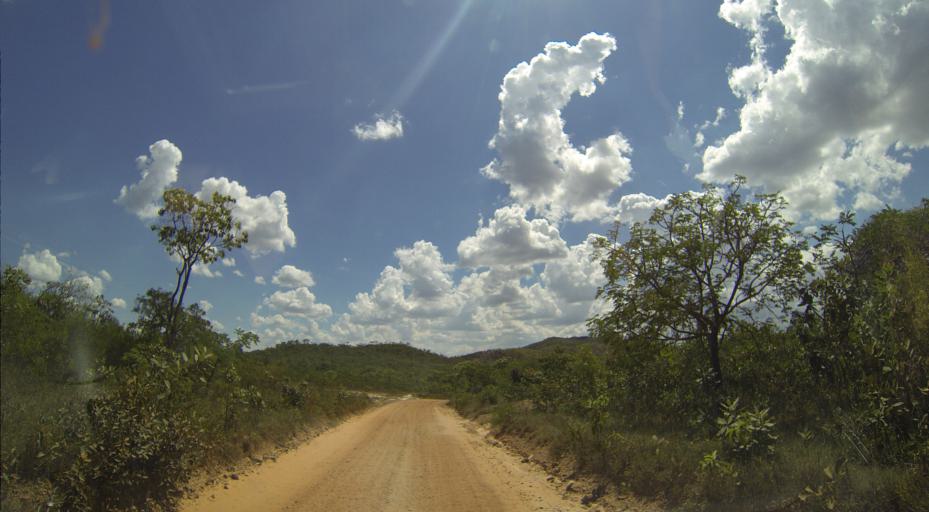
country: BR
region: Minas Gerais
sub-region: Serro
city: Serro
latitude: -18.4926
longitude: -43.4753
